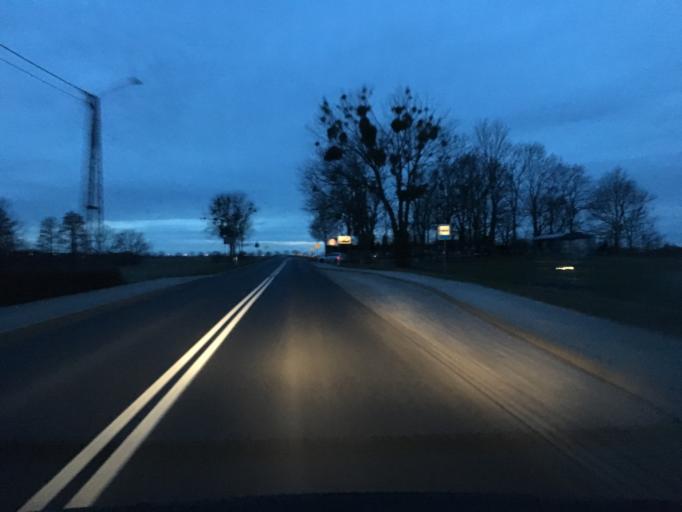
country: PL
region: Opole Voivodeship
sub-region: Powiat brzeski
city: Lewin Brzeski
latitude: 50.7736
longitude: 17.6217
